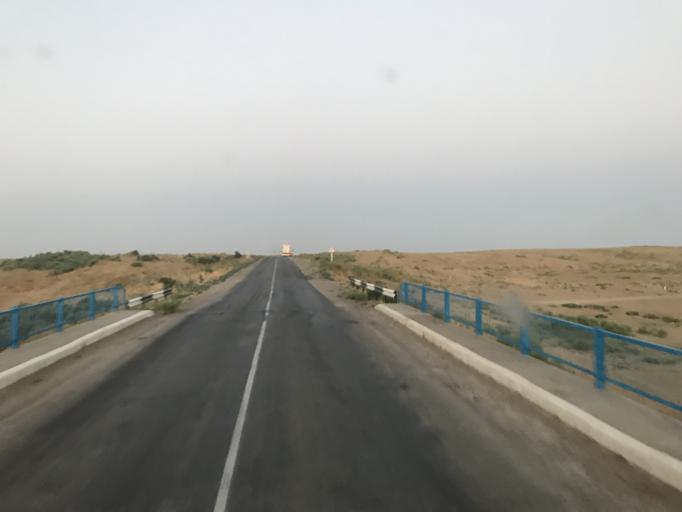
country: UZ
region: Toshkent
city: Chinoz
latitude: 41.1989
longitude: 68.6104
